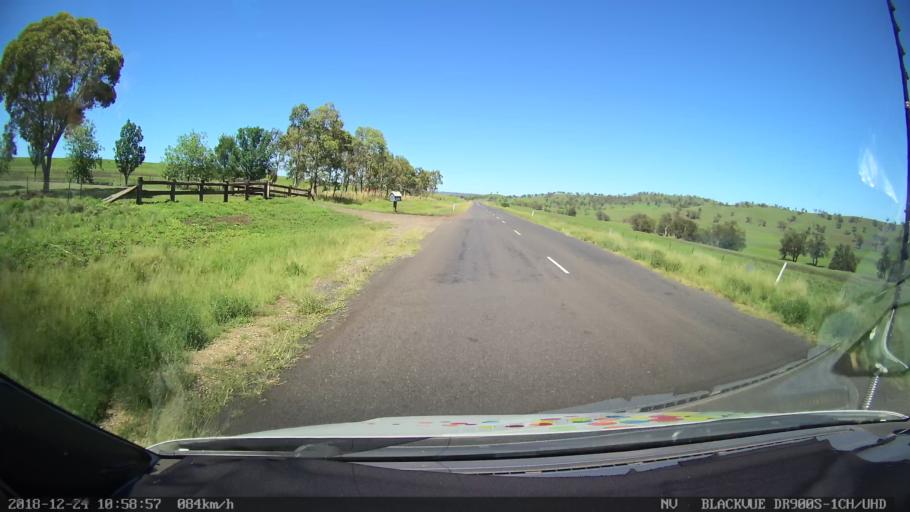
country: AU
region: New South Wales
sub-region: Upper Hunter Shire
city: Merriwa
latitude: -32.0531
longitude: 150.4036
